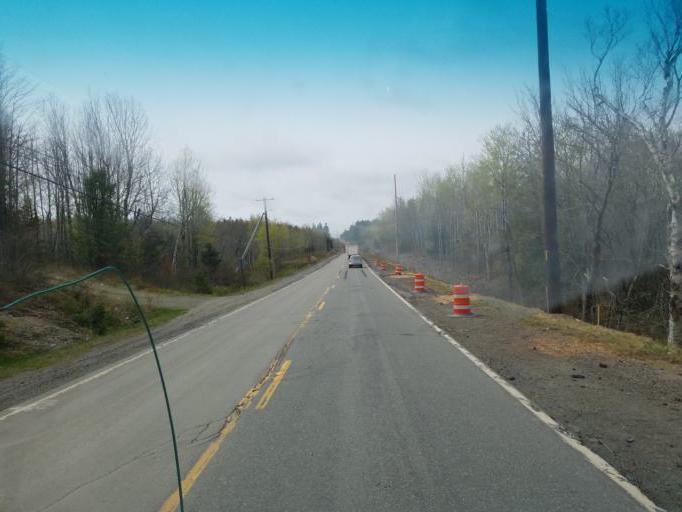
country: US
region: Maine
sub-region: Washington County
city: East Machias
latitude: 44.7788
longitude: -67.1953
